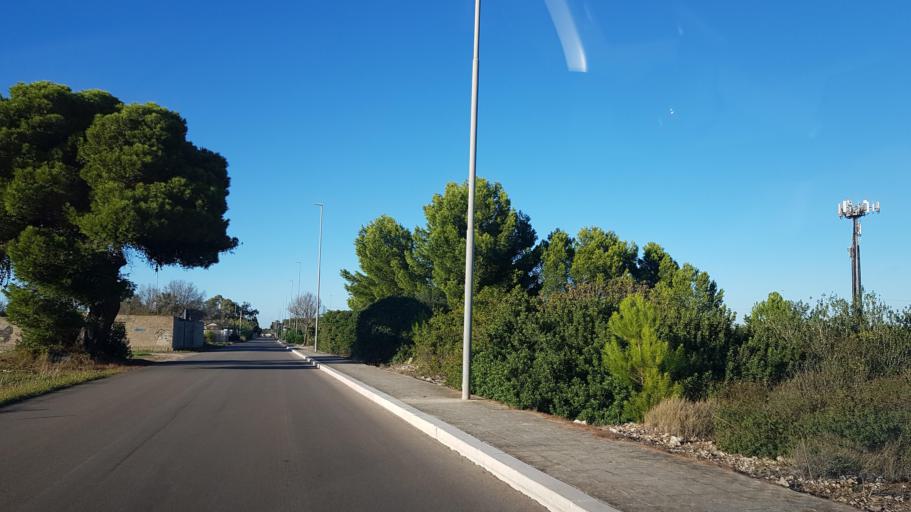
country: IT
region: Apulia
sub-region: Provincia di Lecce
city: Giorgilorio
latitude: 40.4579
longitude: 18.1950
